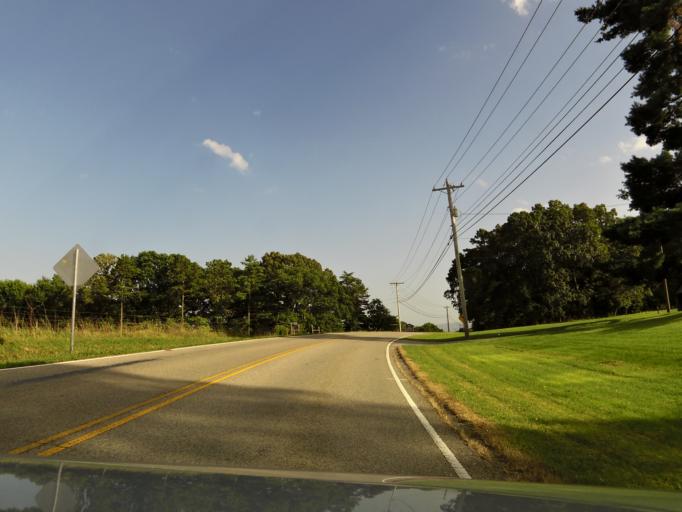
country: US
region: Tennessee
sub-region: Blount County
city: Eagleton Village
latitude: 35.8028
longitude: -83.9068
